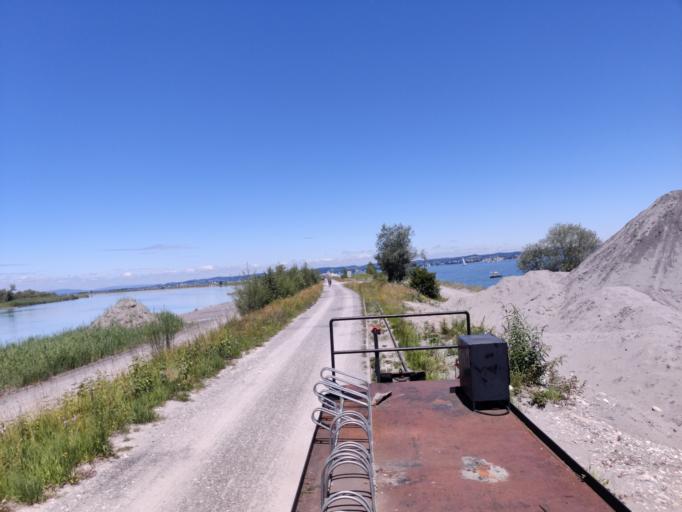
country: AT
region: Vorarlberg
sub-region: Politischer Bezirk Bregenz
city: Hard
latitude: 47.5004
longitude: 9.6719
